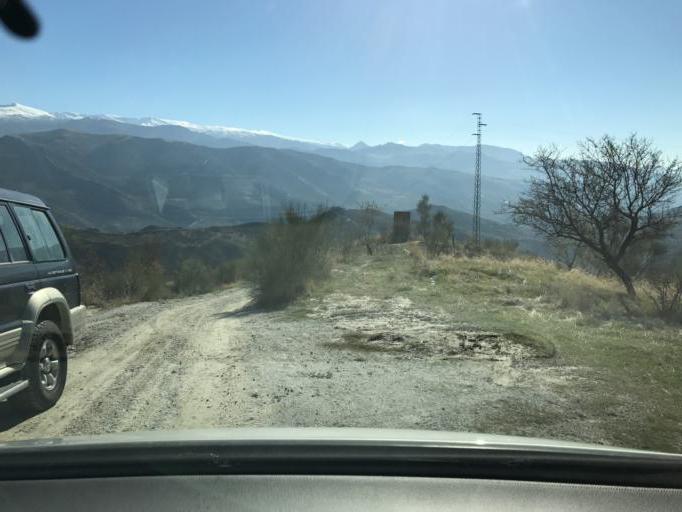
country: ES
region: Andalusia
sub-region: Provincia de Granada
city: Beas de Granada
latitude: 37.2109
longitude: -3.4780
